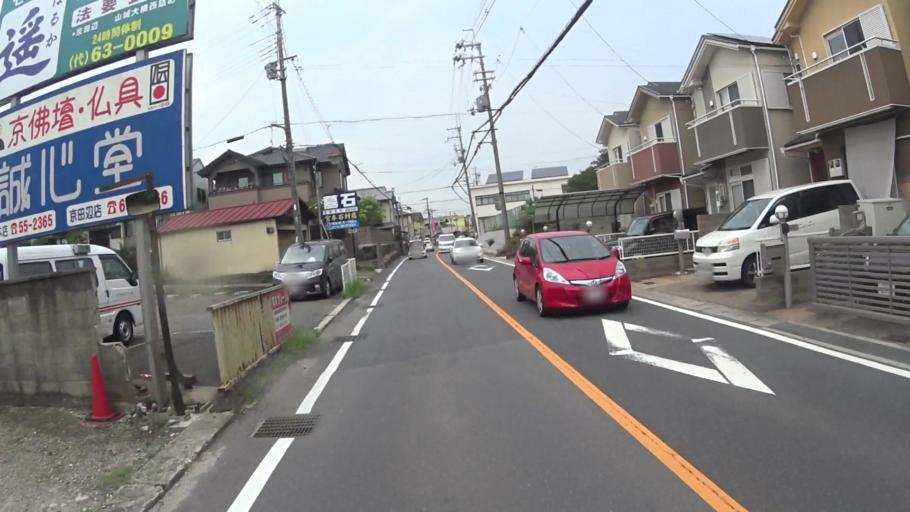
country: JP
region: Kyoto
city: Tanabe
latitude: 34.8293
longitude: 135.7571
